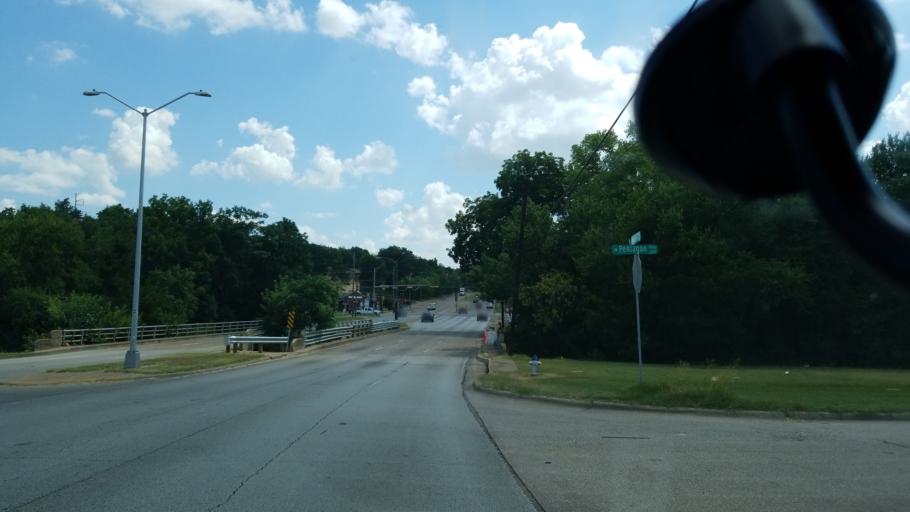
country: US
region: Texas
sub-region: Dallas County
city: Cockrell Hill
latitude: 32.7071
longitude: -96.8745
